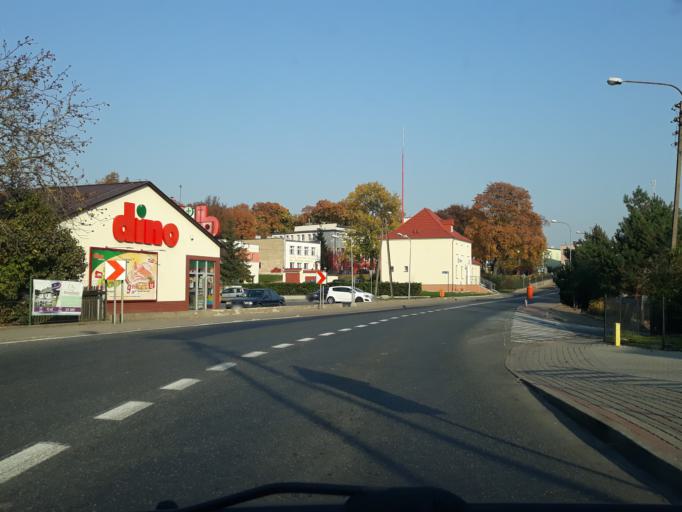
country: PL
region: Kujawsko-Pomorskie
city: Kamien Krajenski
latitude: 53.5329
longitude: 17.5148
